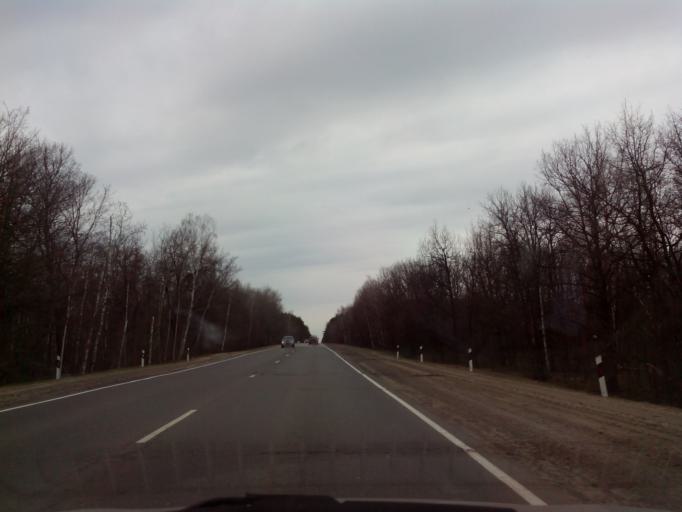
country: RU
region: Tambov
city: Bokino
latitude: 52.5423
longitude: 41.3552
